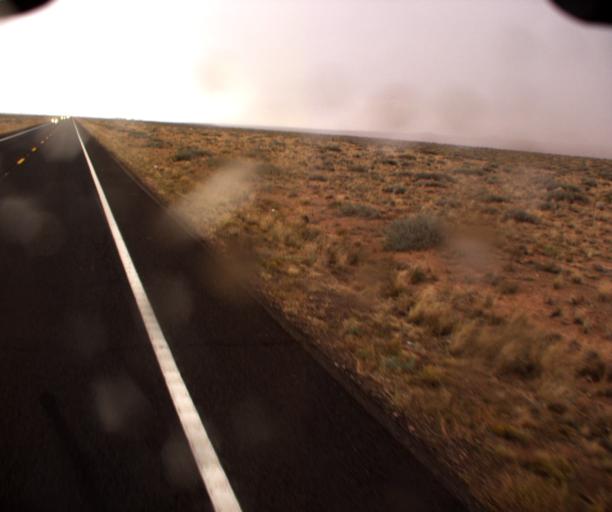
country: US
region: Arizona
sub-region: Coconino County
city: Tuba City
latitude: 36.1619
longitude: -111.1029
